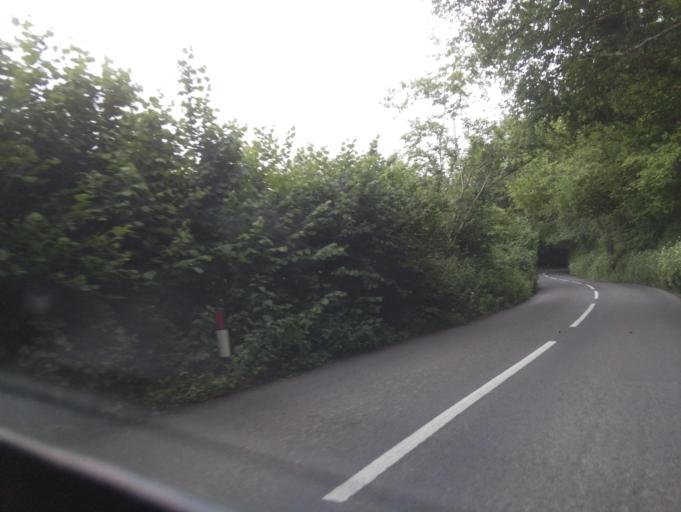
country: GB
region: England
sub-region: Devon
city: Chudleigh
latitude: 50.6419
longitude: -3.6370
